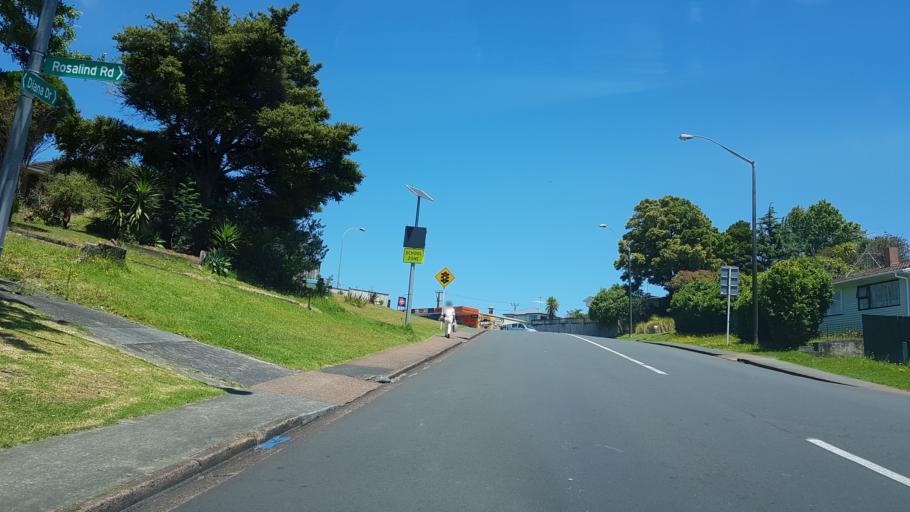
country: NZ
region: Auckland
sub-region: Auckland
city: North Shore
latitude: -36.7788
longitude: 174.7299
